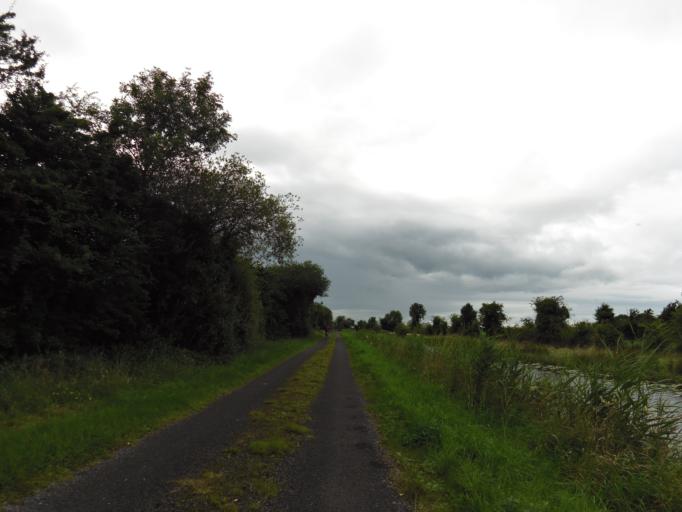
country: IE
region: Leinster
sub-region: An Longfort
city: Edgeworthstown
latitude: 53.5806
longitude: -7.5753
